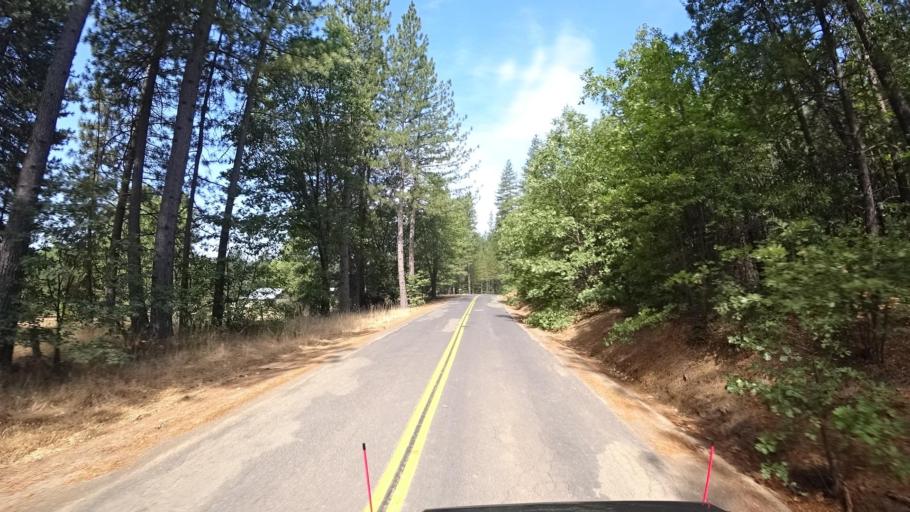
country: US
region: California
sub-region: Tuolumne County
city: Tuolumne City
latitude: 37.7632
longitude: -120.1468
